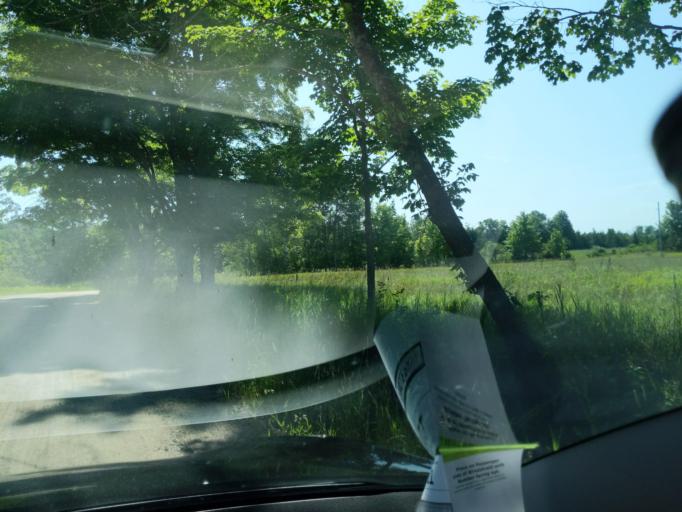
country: US
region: Michigan
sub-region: Cheboygan County
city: Cheboygan
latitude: 45.6536
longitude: -84.6311
